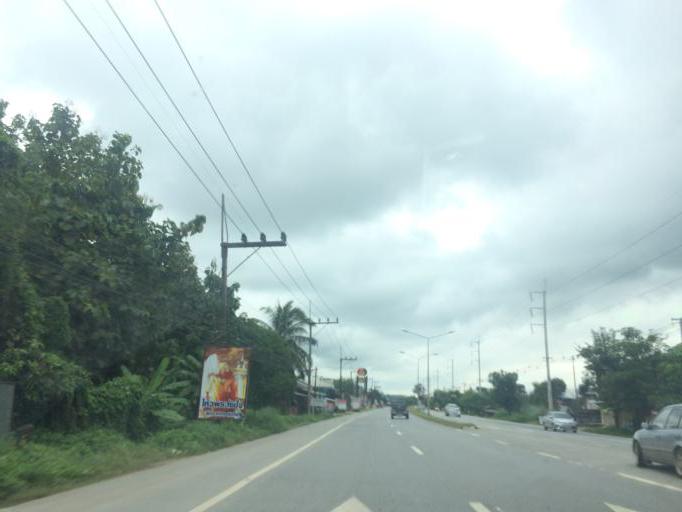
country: TH
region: Chiang Rai
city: Mae Chan
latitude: 20.0800
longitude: 99.8750
